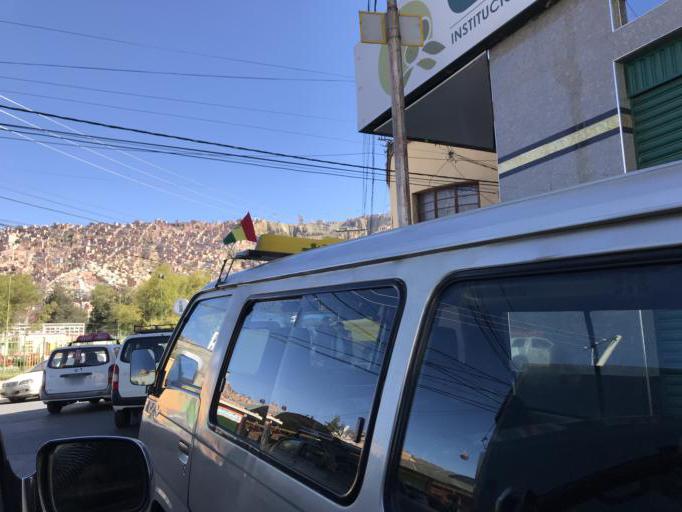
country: BO
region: La Paz
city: La Paz
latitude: -16.4949
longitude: -68.1511
